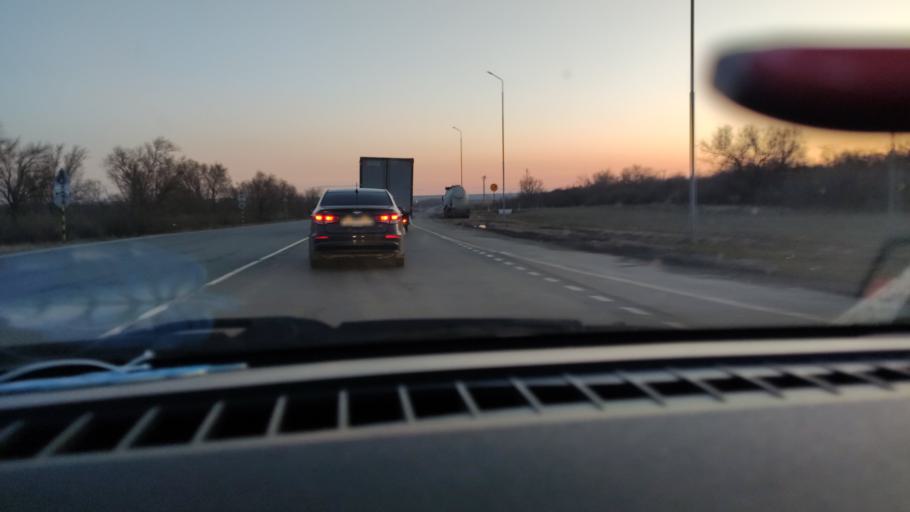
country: RU
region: Saratov
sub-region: Saratovskiy Rayon
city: Saratov
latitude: 51.6819
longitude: 46.0017
